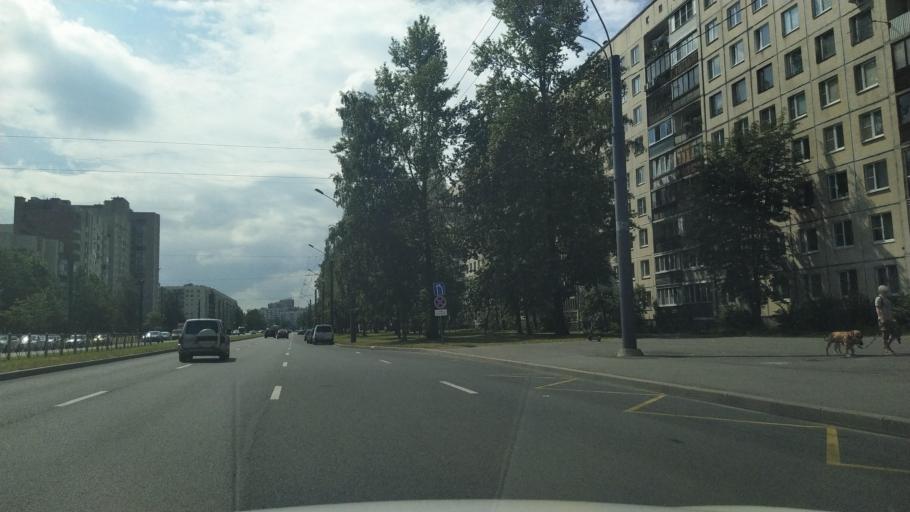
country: RU
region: Leningrad
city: Parnas
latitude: 60.0433
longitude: 30.3493
